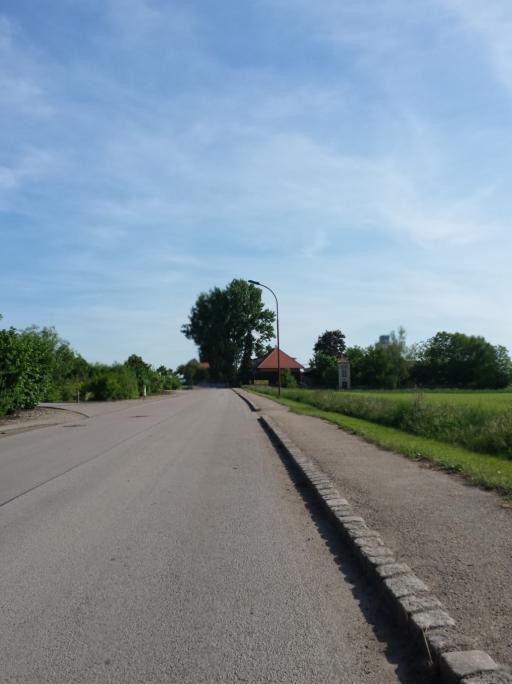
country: AT
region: Lower Austria
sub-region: Politischer Bezirk Hollabrunn
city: Wullersdorf
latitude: 48.6188
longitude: 16.0947
